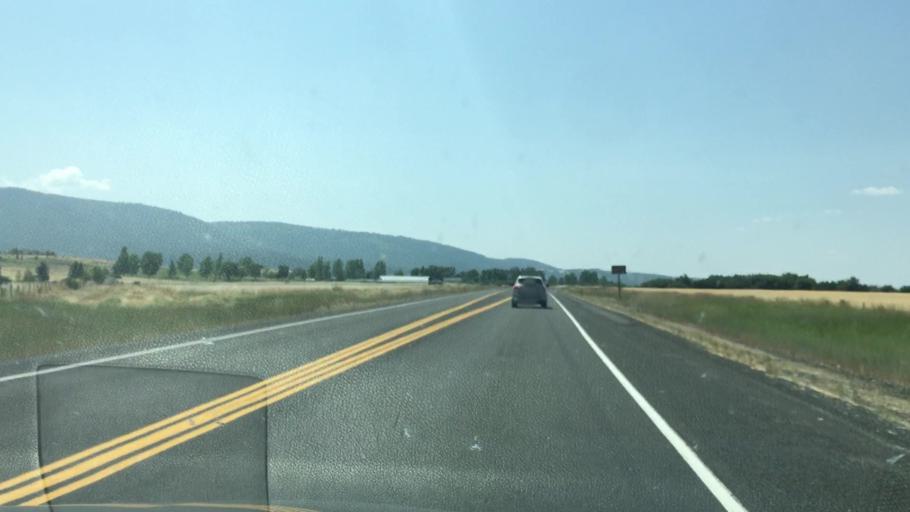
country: US
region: Idaho
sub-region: Idaho County
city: Grangeville
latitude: 45.9203
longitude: -116.1553
